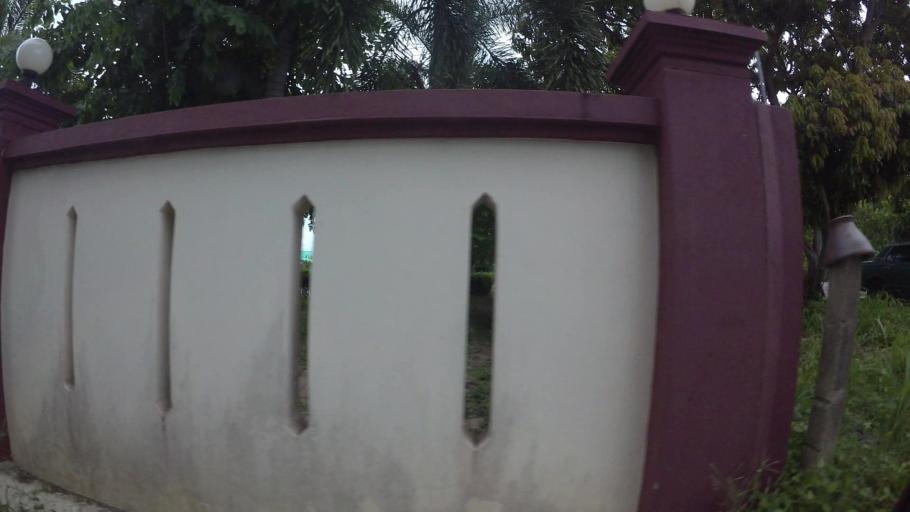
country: TH
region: Chon Buri
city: Sattahip
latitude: 12.6892
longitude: 100.9028
